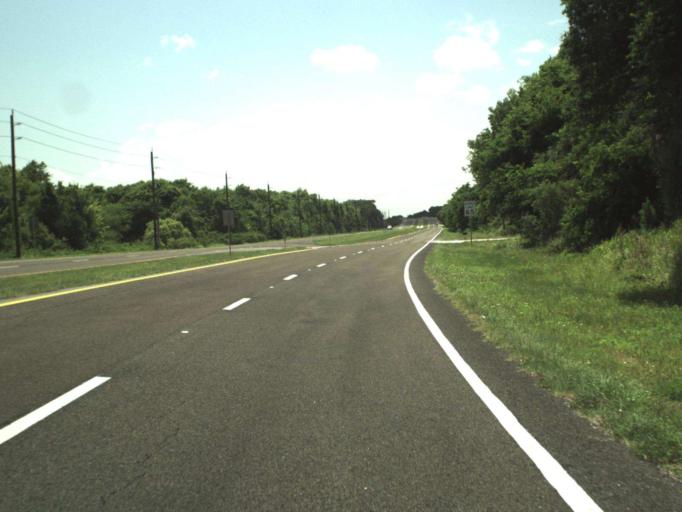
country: US
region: Florida
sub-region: Volusia County
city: Oak Hill
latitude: 28.8307
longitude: -80.8442
